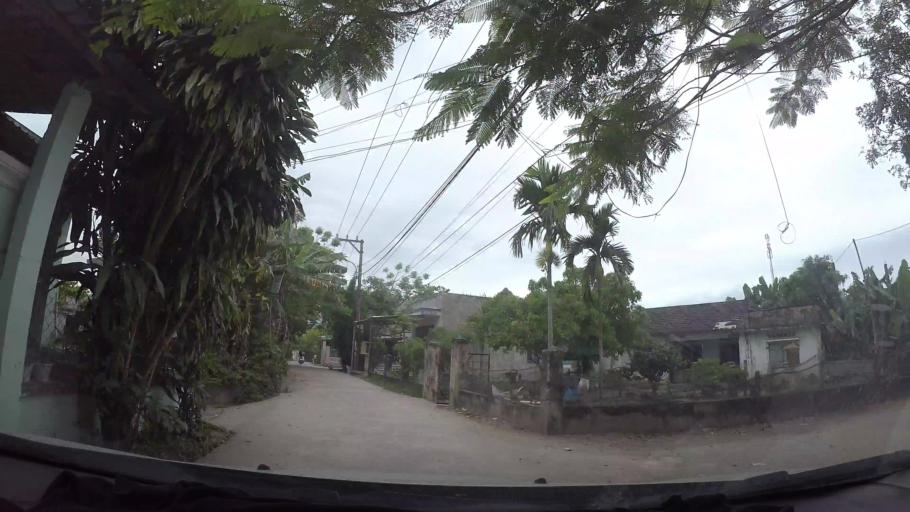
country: VN
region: Da Nang
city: Lien Chieu
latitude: 16.0887
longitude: 108.1023
